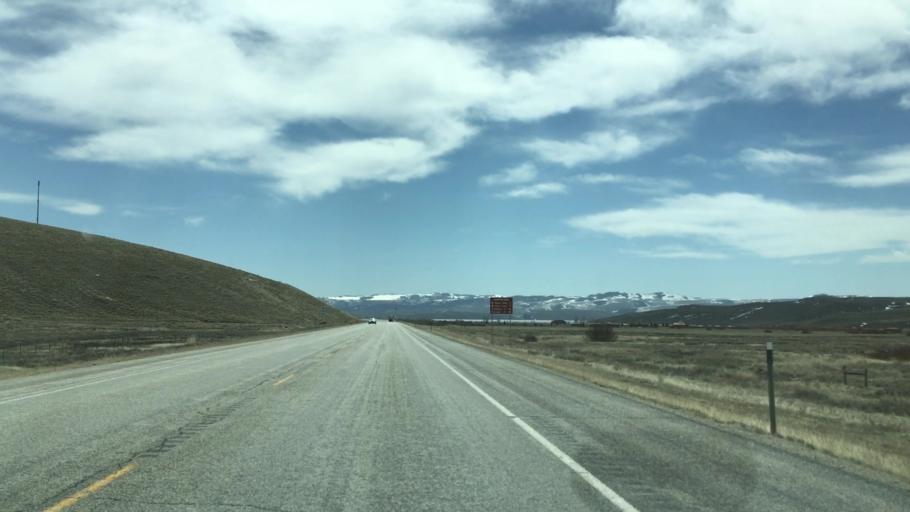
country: US
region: Utah
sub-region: Wasatch County
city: Heber
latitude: 40.2470
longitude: -111.1899
